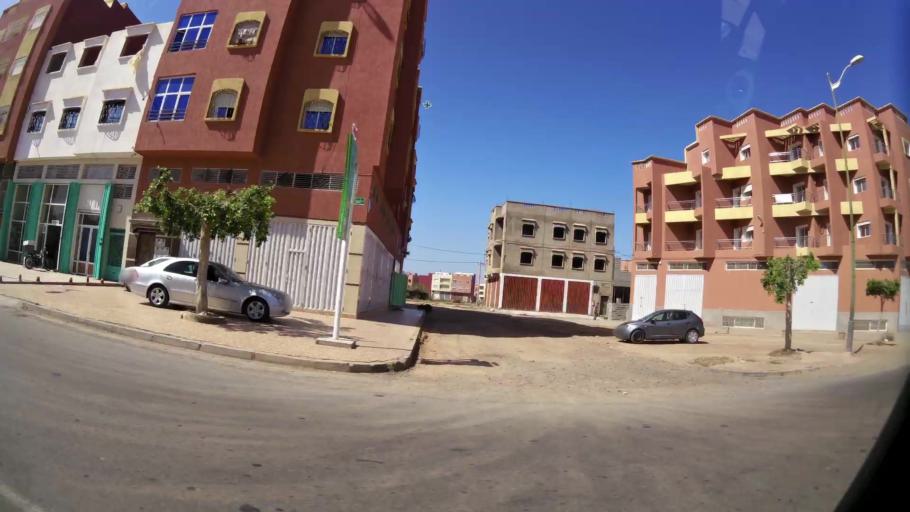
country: MA
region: Souss-Massa-Draa
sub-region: Inezgane-Ait Mellou
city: Inezgane
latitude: 30.3398
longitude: -9.5067
